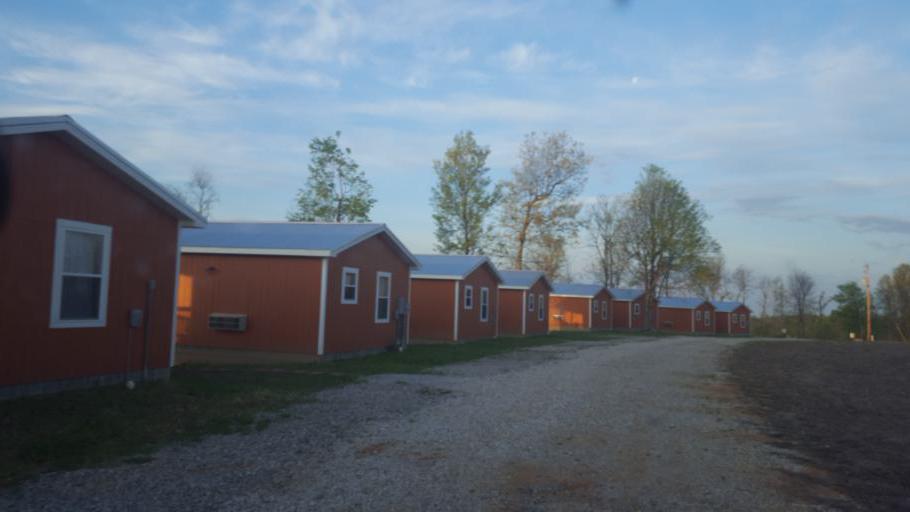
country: US
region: Kentucky
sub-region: Barren County
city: Cave City
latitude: 37.1353
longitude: -86.0001
